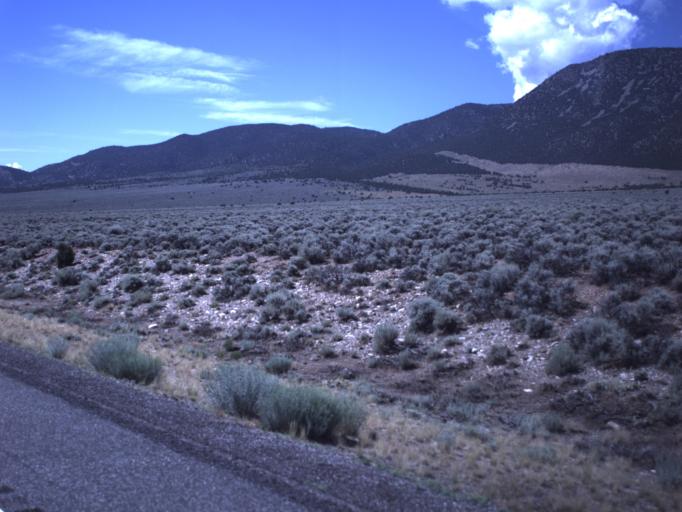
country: US
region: Utah
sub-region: Piute County
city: Junction
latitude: 38.3773
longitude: -112.2272
